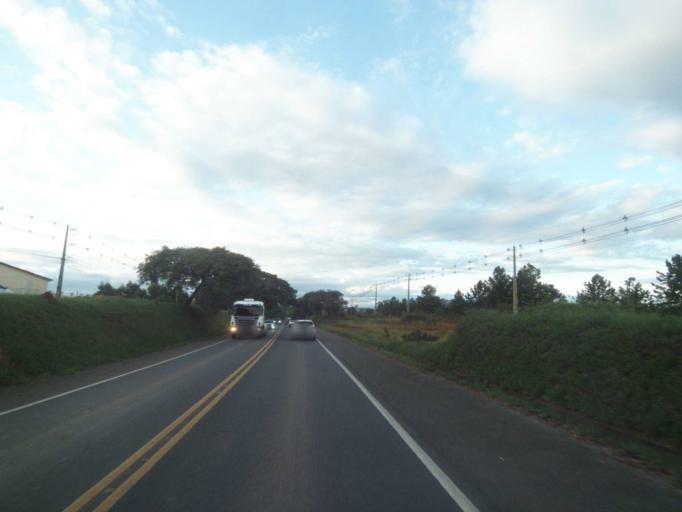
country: BR
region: Parana
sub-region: Telemaco Borba
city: Telemaco Borba
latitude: -24.3558
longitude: -50.6586
